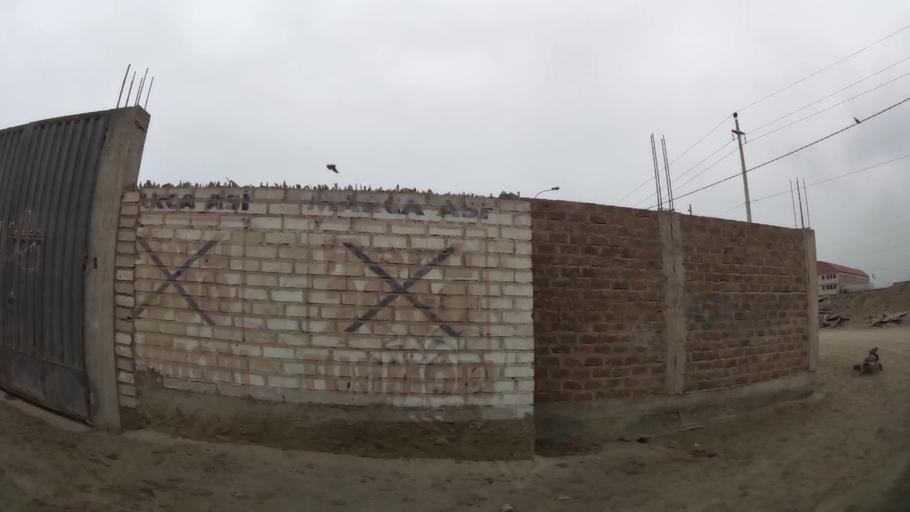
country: PE
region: Lima
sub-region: Lima
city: Punta Hermosa
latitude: -12.3140
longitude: -76.8334
